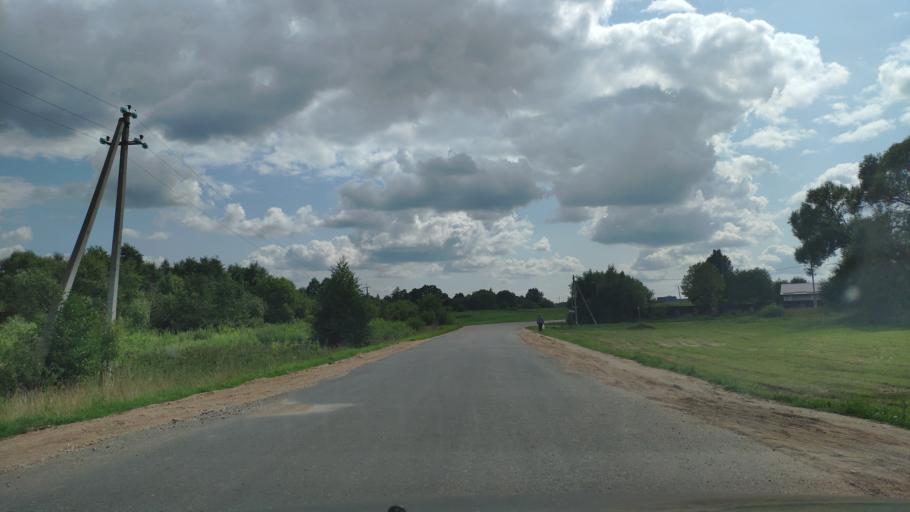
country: BY
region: Minsk
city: Khatsyezhyna
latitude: 53.8662
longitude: 27.3170
